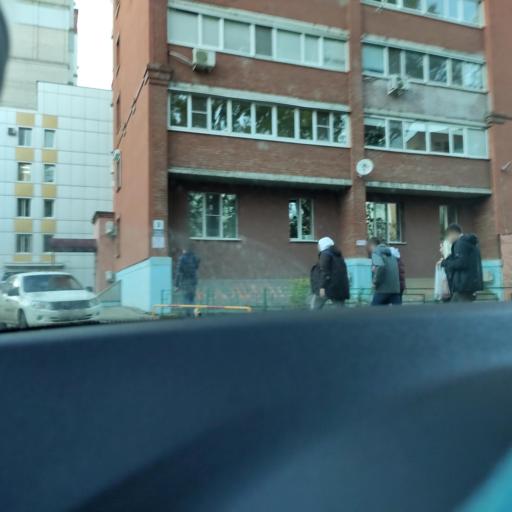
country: RU
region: Samara
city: Samara
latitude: 53.2182
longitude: 50.2474
